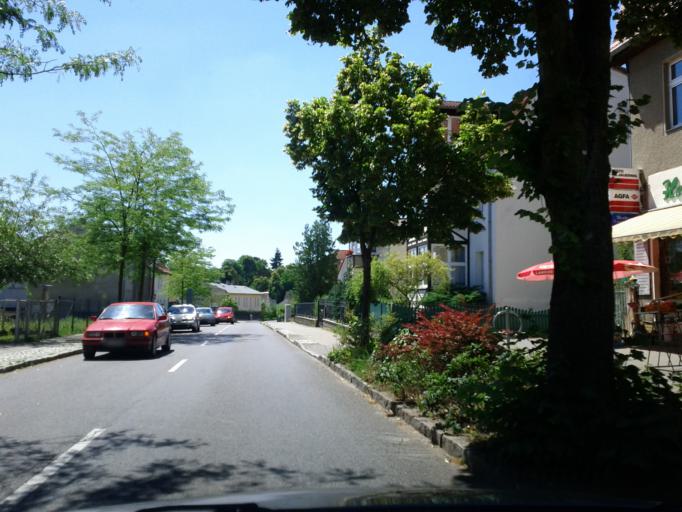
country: DE
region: Brandenburg
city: Grunheide
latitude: 52.4244
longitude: 13.8224
